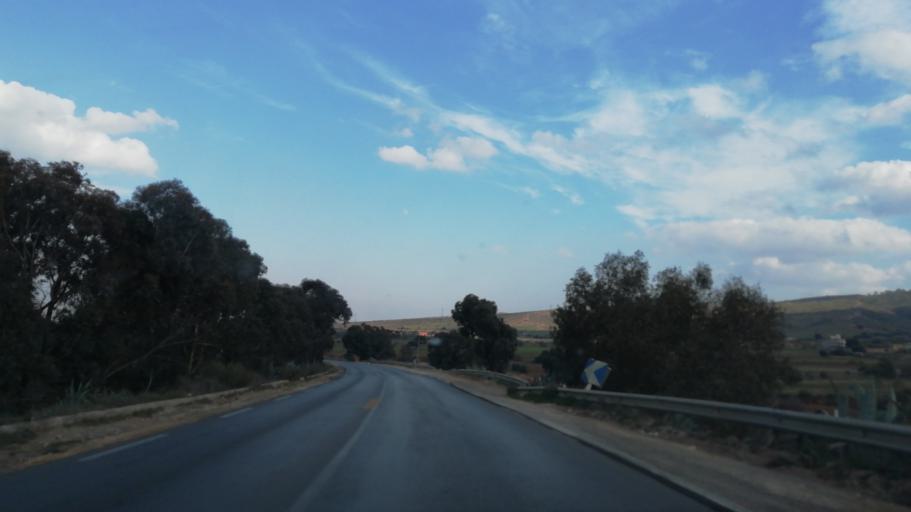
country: DZ
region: Relizane
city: Relizane
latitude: 35.9023
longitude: 0.4511
